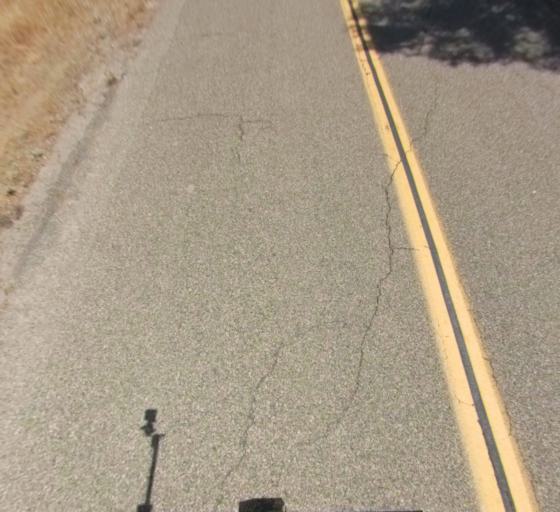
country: US
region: California
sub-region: Fresno County
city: Auberry
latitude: 37.1540
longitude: -119.5129
